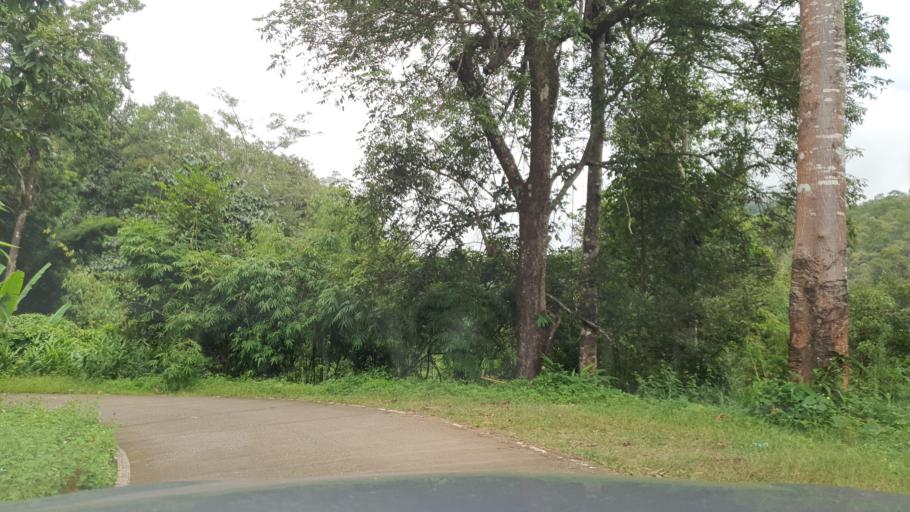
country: TH
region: Chiang Mai
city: Mae Taeng
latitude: 19.2363
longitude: 98.9316
